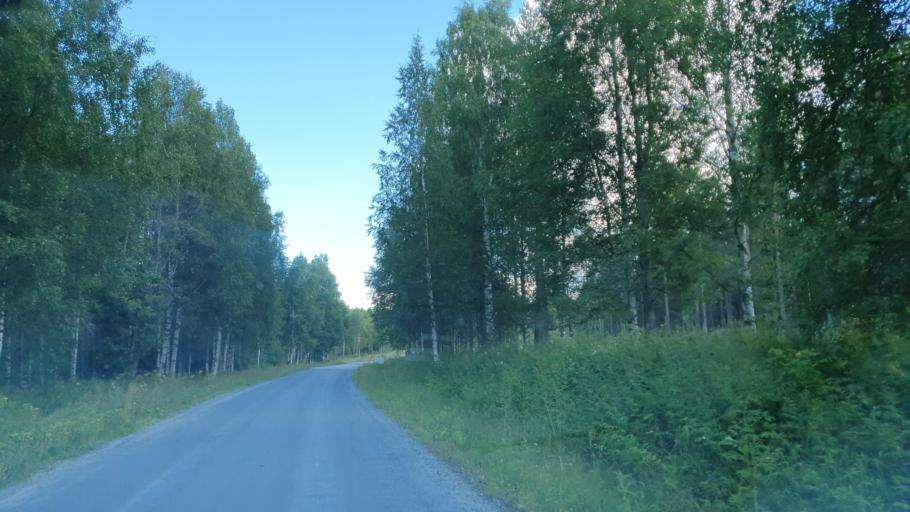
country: FI
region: Kainuu
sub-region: Kehys-Kainuu
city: Kuhmo
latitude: 64.0949
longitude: 29.4206
